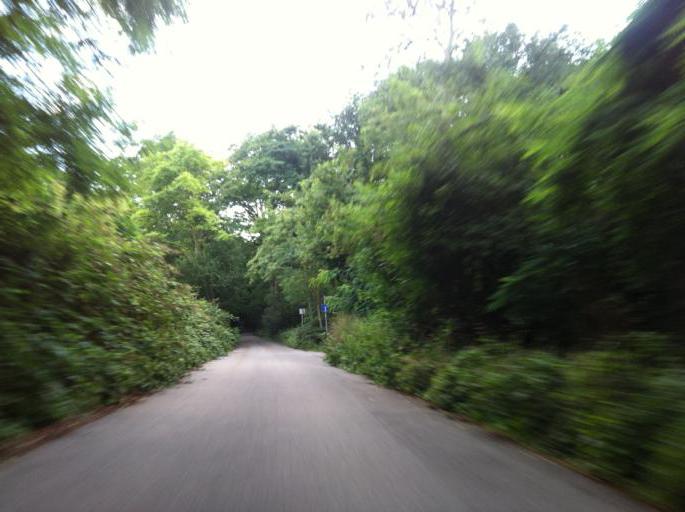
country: DE
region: North Rhine-Westphalia
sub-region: Regierungsbezirk Koln
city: Poll
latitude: 50.9064
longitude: 7.0094
